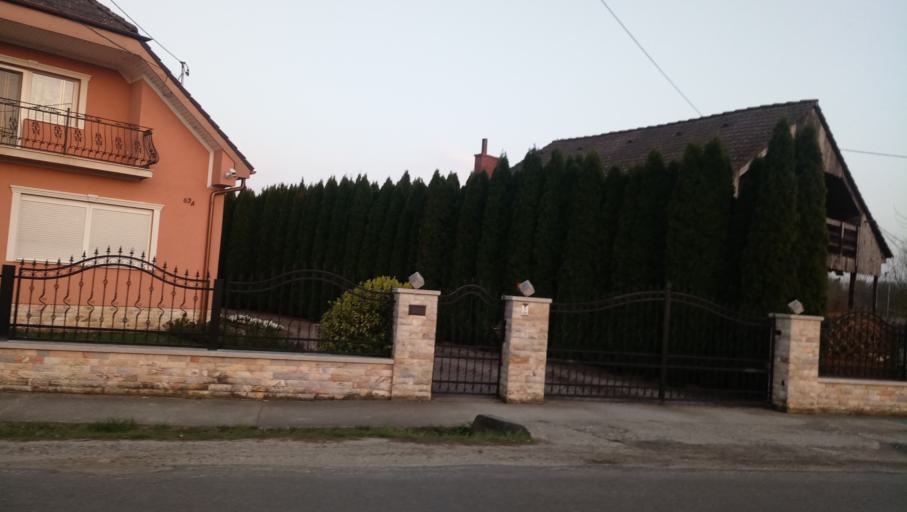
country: HU
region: Somogy
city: Nagybajom
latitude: 46.4193
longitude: 17.5975
